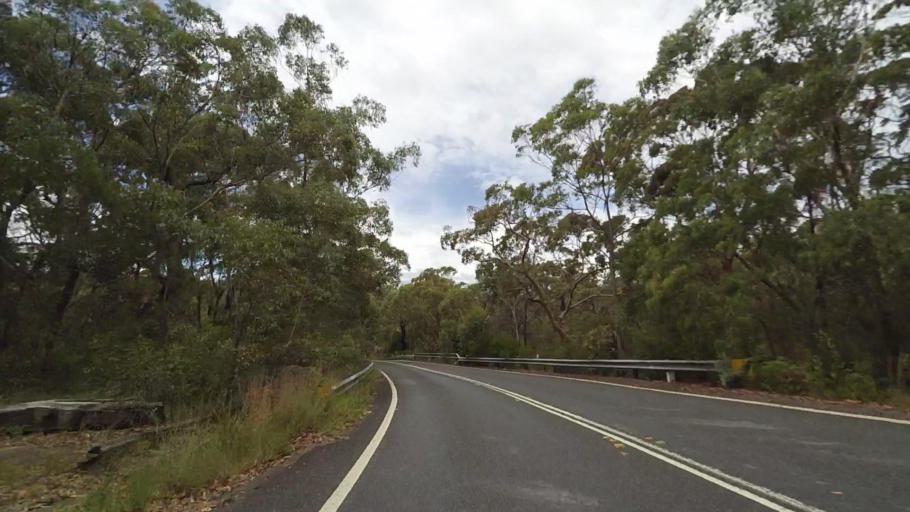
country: AU
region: New South Wales
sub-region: Sutherland Shire
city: Grays Point
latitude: -34.1143
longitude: 151.0662
